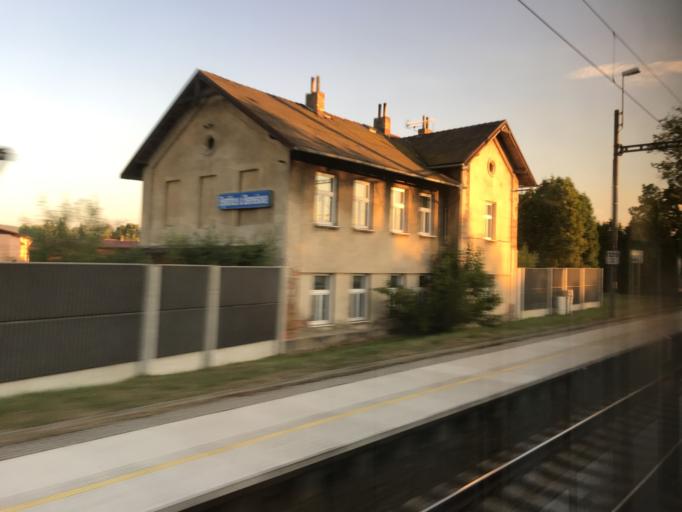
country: CZ
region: Central Bohemia
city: Bystrice
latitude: 49.7422
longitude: 14.6674
